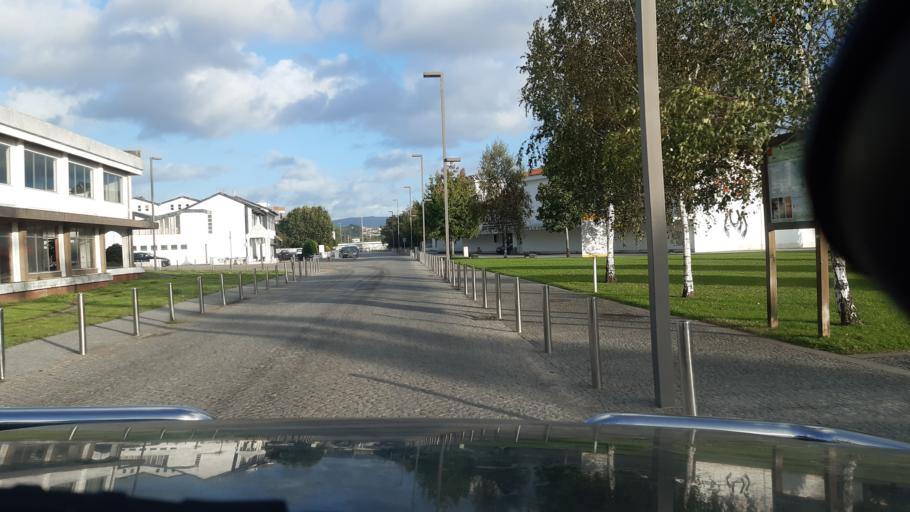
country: PT
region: Aveiro
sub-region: Agueda
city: Agueda
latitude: 40.5729
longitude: -8.4530
